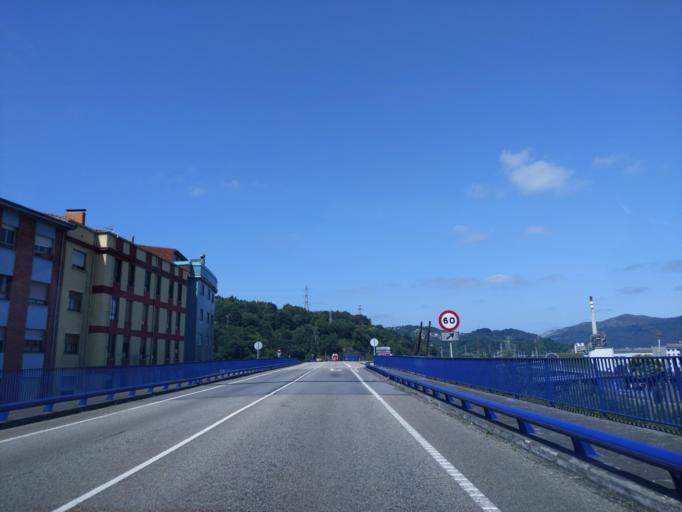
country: ES
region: Asturias
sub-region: Province of Asturias
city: Sama
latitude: 43.2988
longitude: -5.6853
